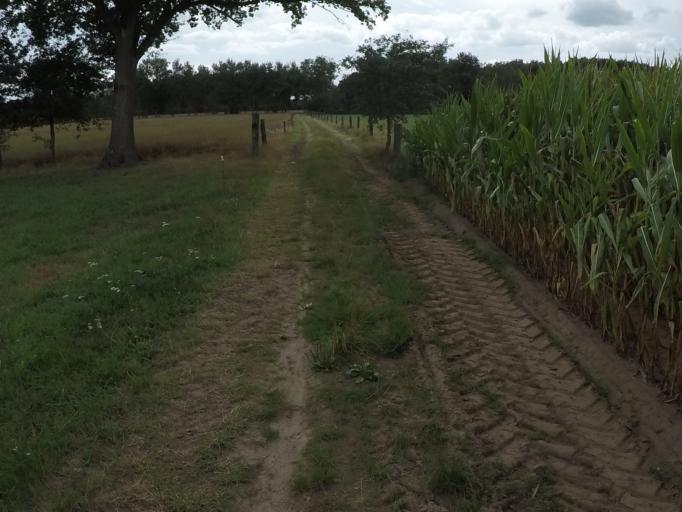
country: BE
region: Flanders
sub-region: Provincie Antwerpen
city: Vorselaar
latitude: 51.2232
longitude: 4.7766
